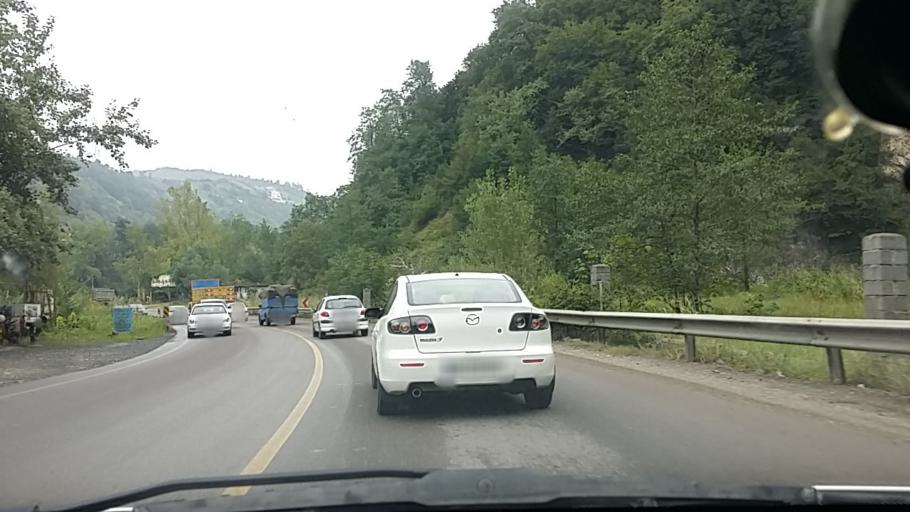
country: IR
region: Mazandaran
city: Chalus
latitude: 36.6123
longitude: 51.3895
